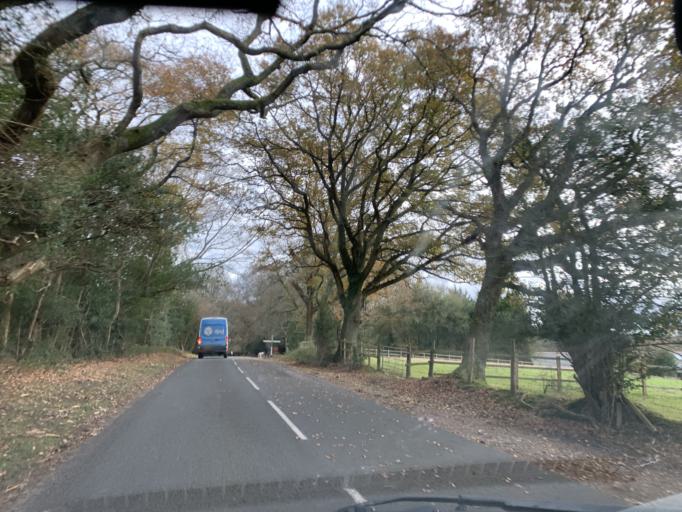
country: GB
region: England
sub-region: Hampshire
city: Lyndhurst
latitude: 50.8912
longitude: -1.6169
